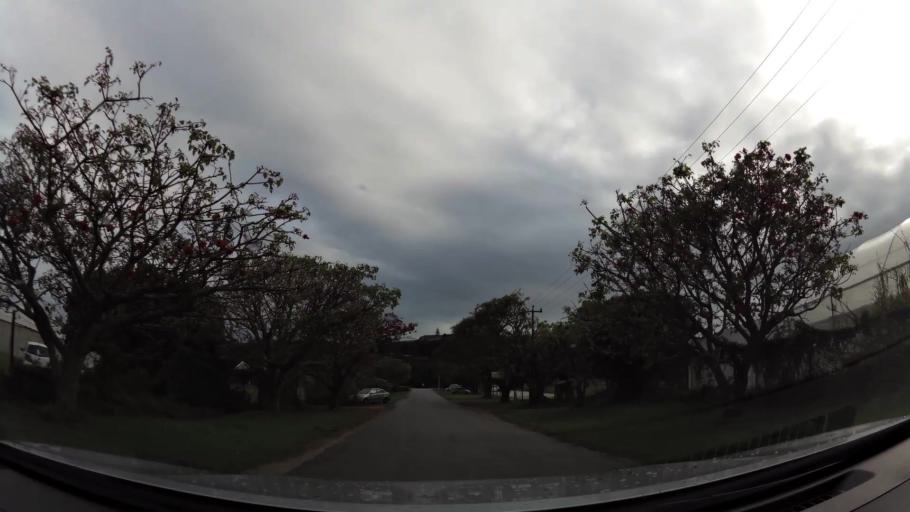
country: ZA
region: Eastern Cape
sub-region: Nelson Mandela Bay Metropolitan Municipality
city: Port Elizabeth
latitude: -34.0123
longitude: 25.4969
